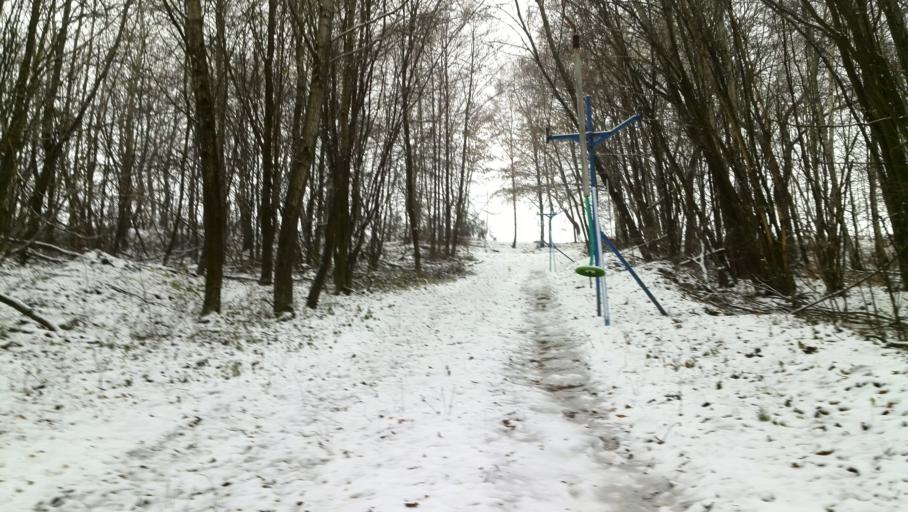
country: SK
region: Presovsky
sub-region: Okres Presov
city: Presov
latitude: 48.9359
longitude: 21.1711
